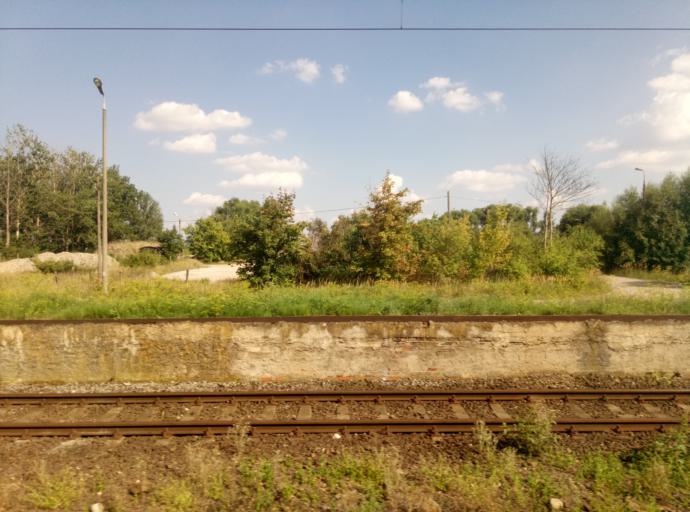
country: PL
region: Kujawsko-Pomorskie
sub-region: Powiat wabrzeski
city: Wabrzezno
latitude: 53.2599
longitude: 18.9769
